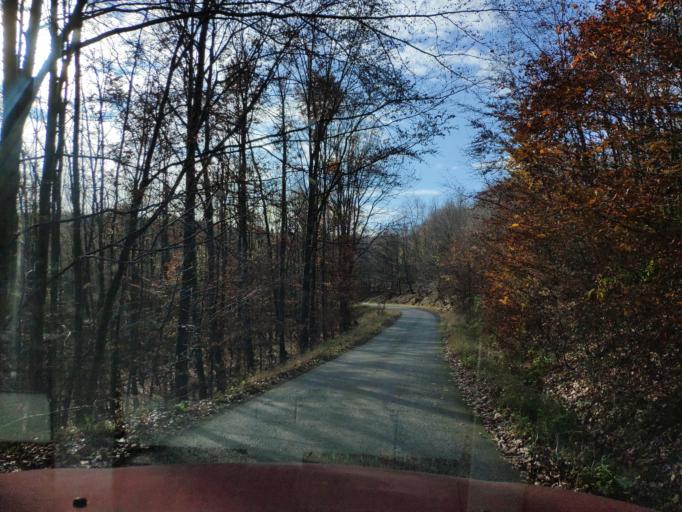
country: SK
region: Kosicky
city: Secovce
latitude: 48.6102
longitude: 21.4571
